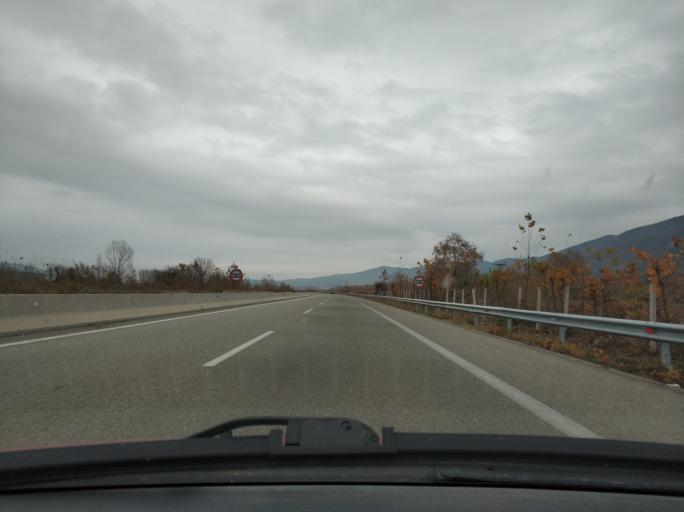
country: GR
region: East Macedonia and Thrace
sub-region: Nomos Kavalas
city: Eleftheres
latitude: 40.8682
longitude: 24.1953
